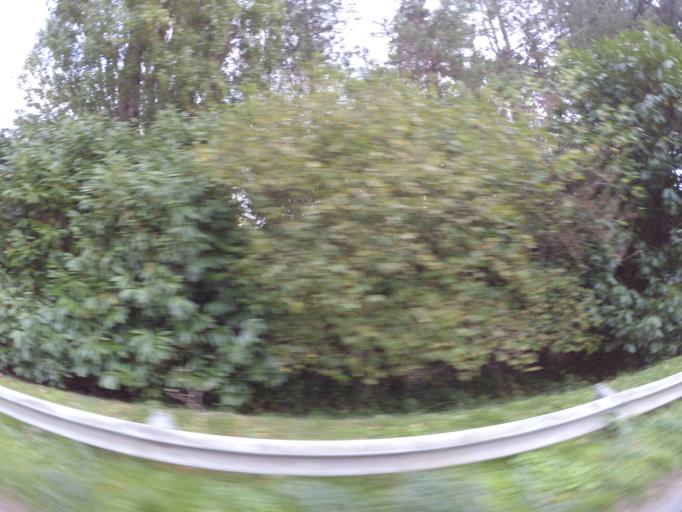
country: FR
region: Centre
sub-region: Departement d'Indre-et-Loire
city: Vernou-sur-Brenne
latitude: 47.4437
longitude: 0.8636
